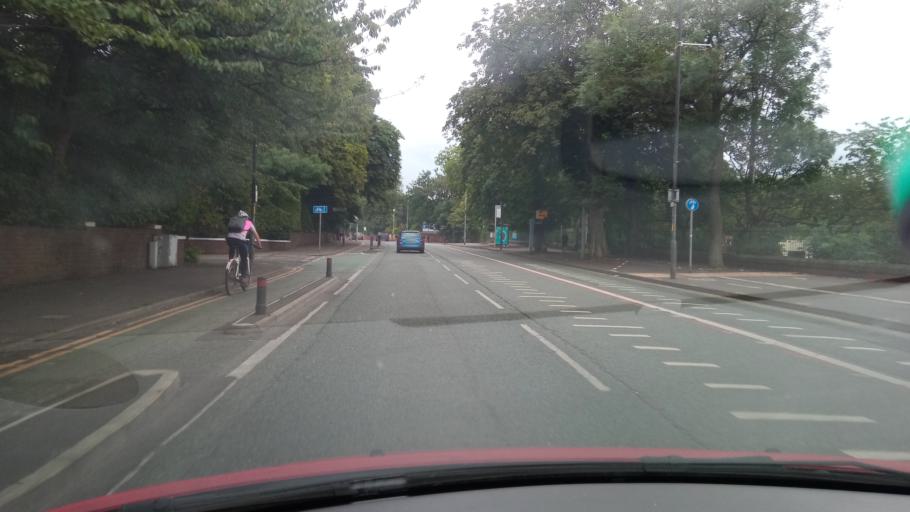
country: GB
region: England
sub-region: Manchester
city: Fallowfield
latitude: 53.4491
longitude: -2.2203
